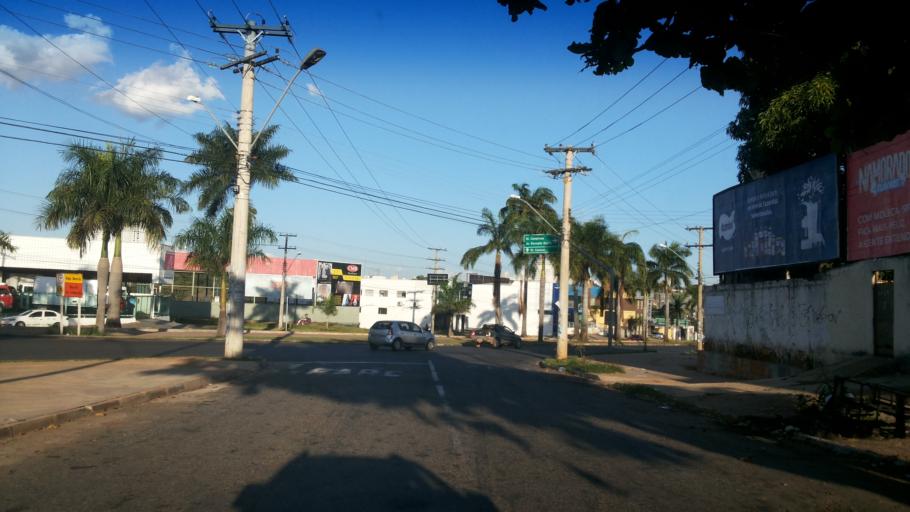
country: BR
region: Goias
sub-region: Goiania
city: Goiania
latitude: -16.6519
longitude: -49.2645
